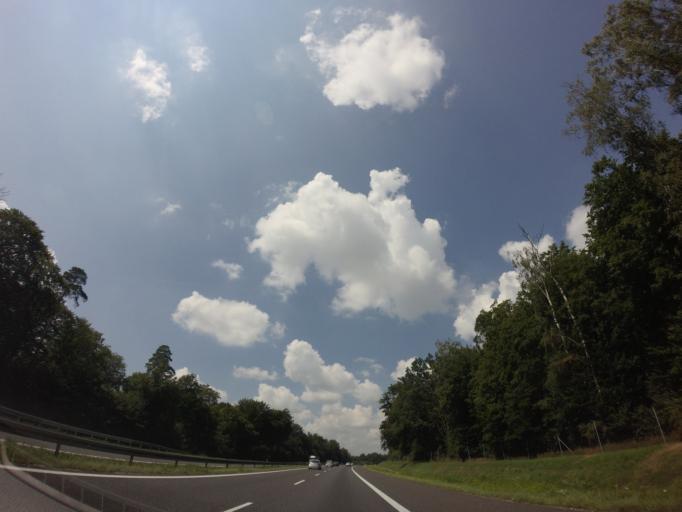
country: PL
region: Opole Voivodeship
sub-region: Powiat strzelecki
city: Ujazd
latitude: 50.4310
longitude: 18.3737
